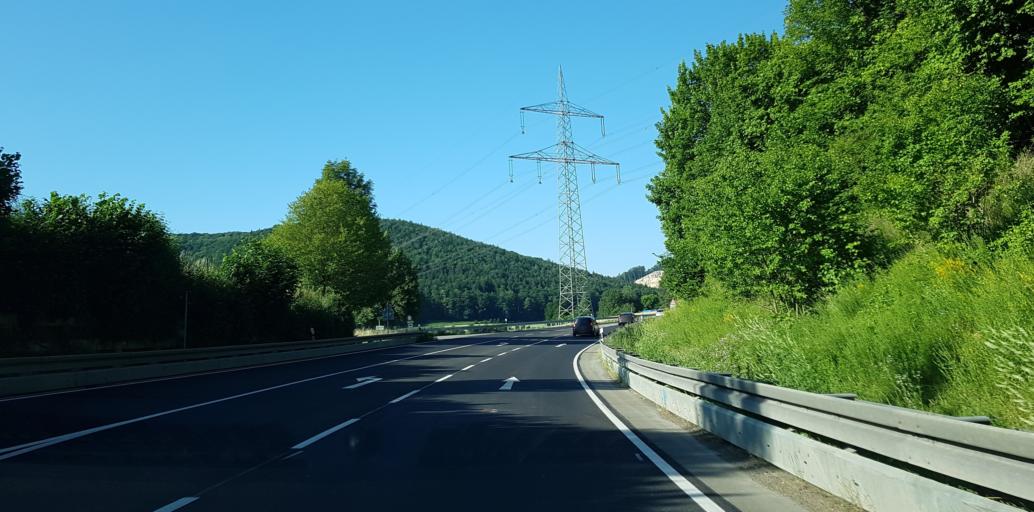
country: DE
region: Baden-Wuerttemberg
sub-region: Tuebingen Region
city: Blaubeuren
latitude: 48.4064
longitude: 9.8326
